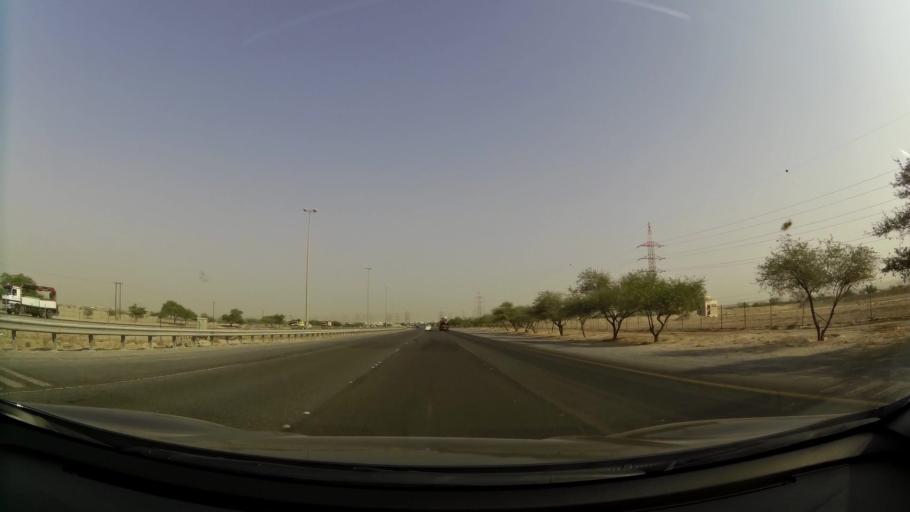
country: KW
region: Al Asimah
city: Ar Rabiyah
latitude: 29.2236
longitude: 47.8853
